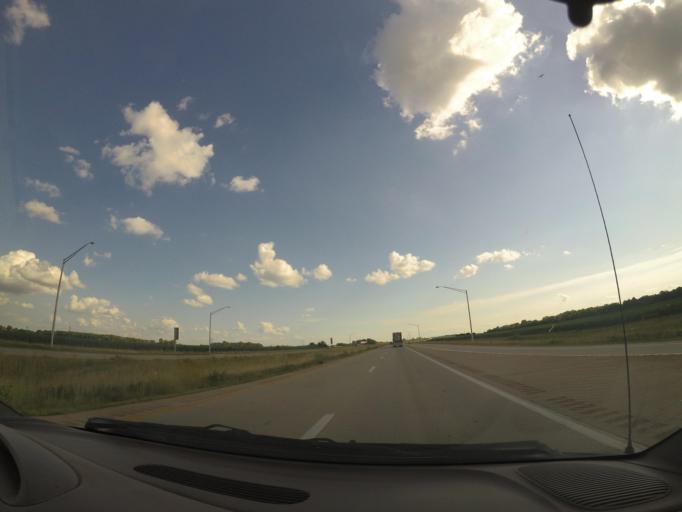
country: US
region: Ohio
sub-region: Lucas County
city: Waterville
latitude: 41.5058
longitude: -83.7561
